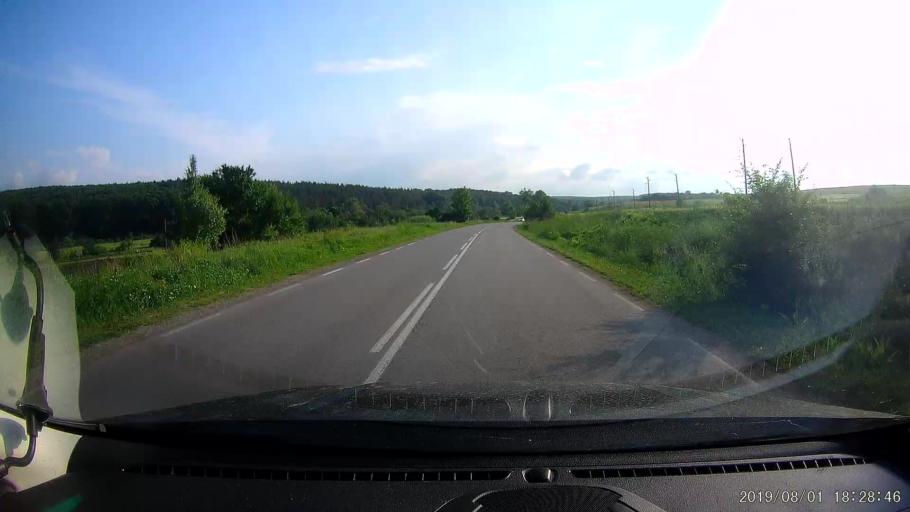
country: BG
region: Shumen
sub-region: Obshtina Venets
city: Venets
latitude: 43.5703
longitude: 26.9571
